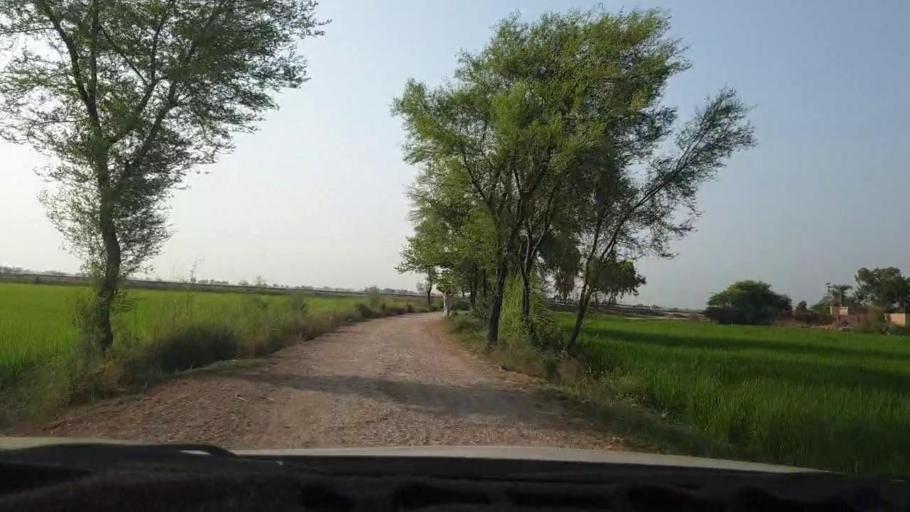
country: PK
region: Sindh
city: Larkana
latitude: 27.5033
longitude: 68.1752
